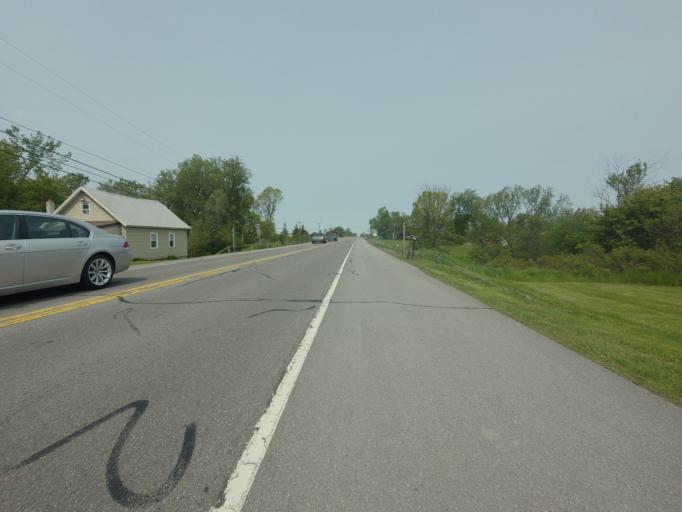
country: US
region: New York
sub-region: Jefferson County
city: Dexter
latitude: 44.0297
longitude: -76.0487
